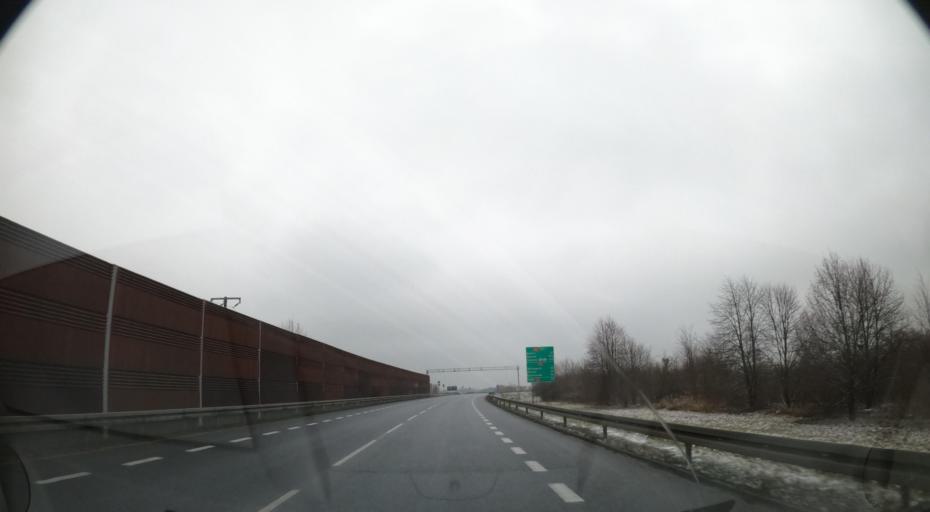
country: PL
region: Masovian Voivodeship
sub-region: Powiat sochaczewski
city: Sochaczew
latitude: 52.2086
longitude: 20.2487
